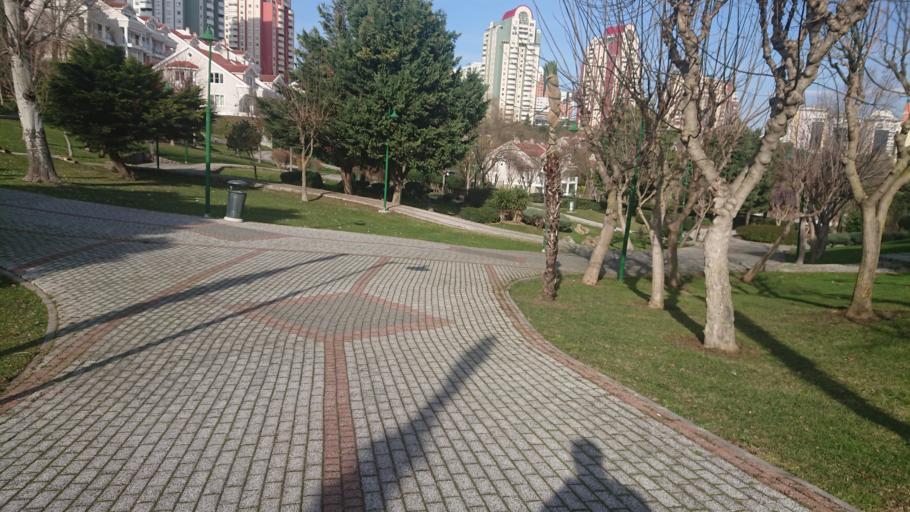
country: TR
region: Istanbul
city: Esenyurt
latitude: 41.0683
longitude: 28.6797
